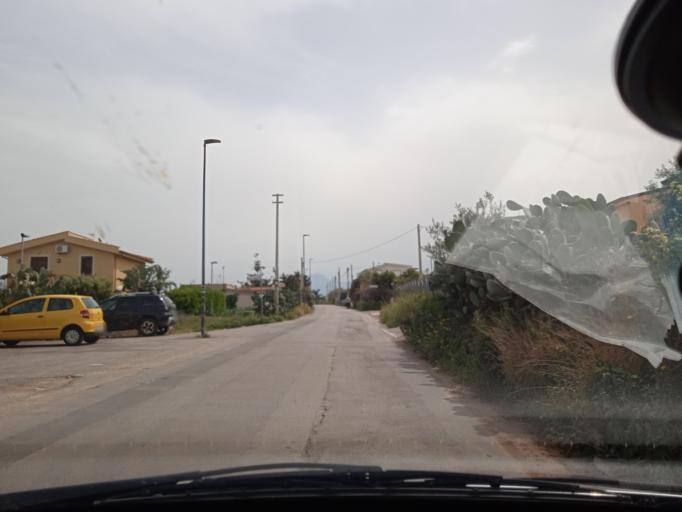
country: IT
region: Sicily
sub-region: Palermo
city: Torre Colonna-Sperone
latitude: 38.0306
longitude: 13.5680
